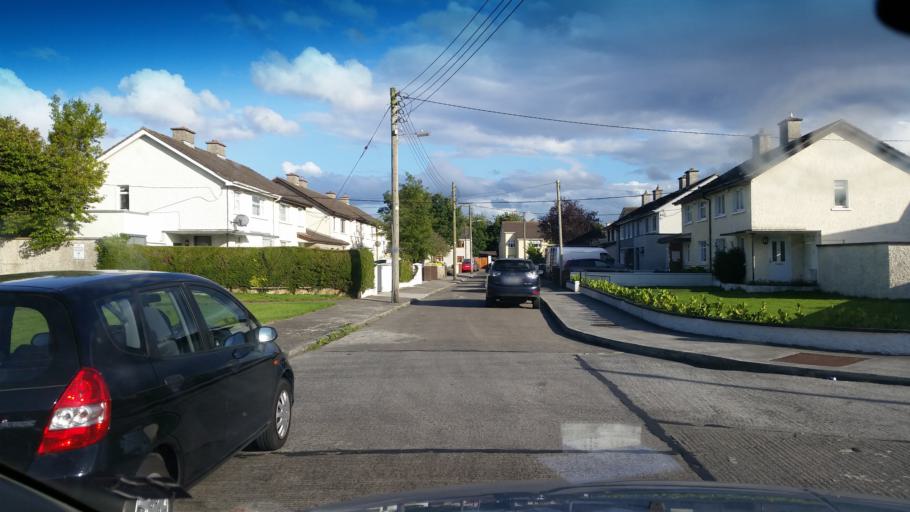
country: IE
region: Leinster
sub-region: Fingal County
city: Blanchardstown
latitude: 53.3841
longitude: -6.3771
